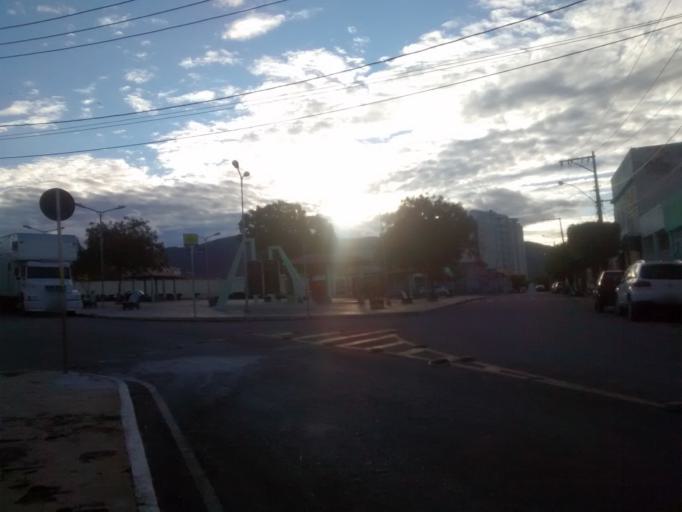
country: BR
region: Bahia
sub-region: Brumado
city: Brumado
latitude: -14.2034
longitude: -41.6678
